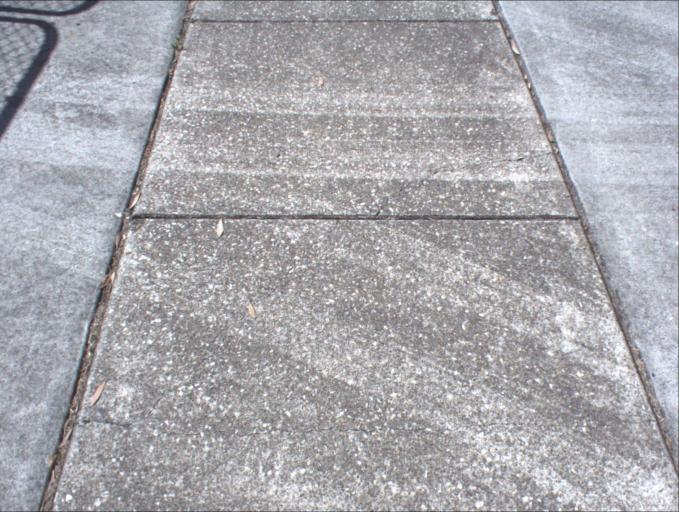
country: AU
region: Queensland
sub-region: Logan
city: Beenleigh
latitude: -27.6876
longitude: 153.2157
